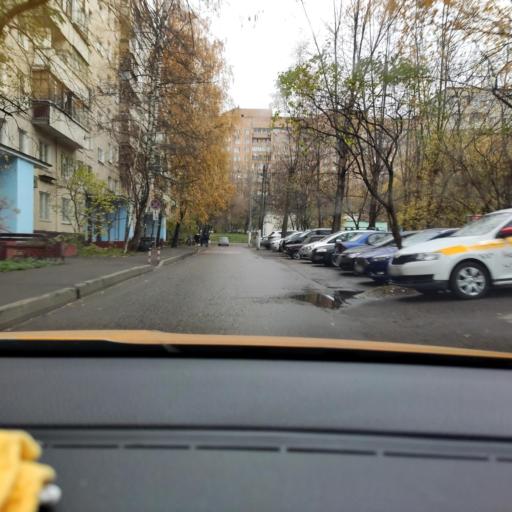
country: RU
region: Moscow
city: Otradnoye
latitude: 55.8711
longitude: 37.6011
